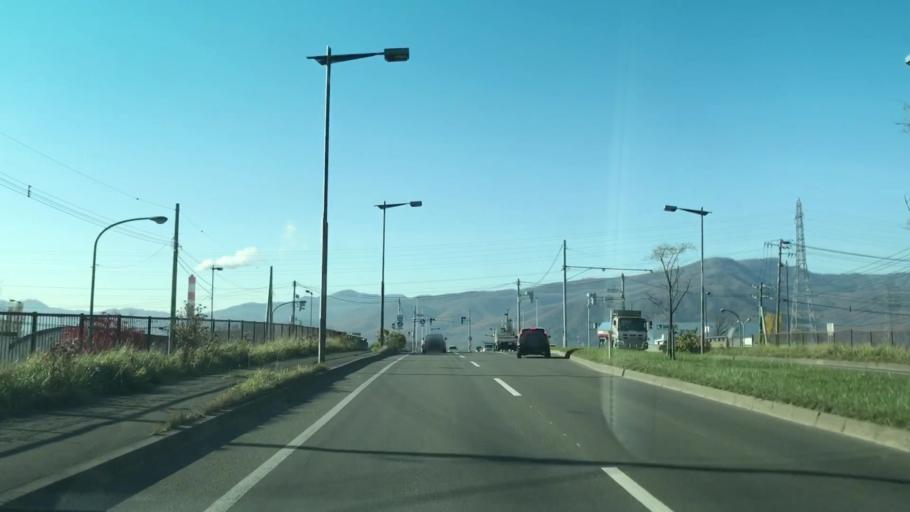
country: JP
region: Hokkaido
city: Sapporo
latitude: 43.1181
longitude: 141.2878
